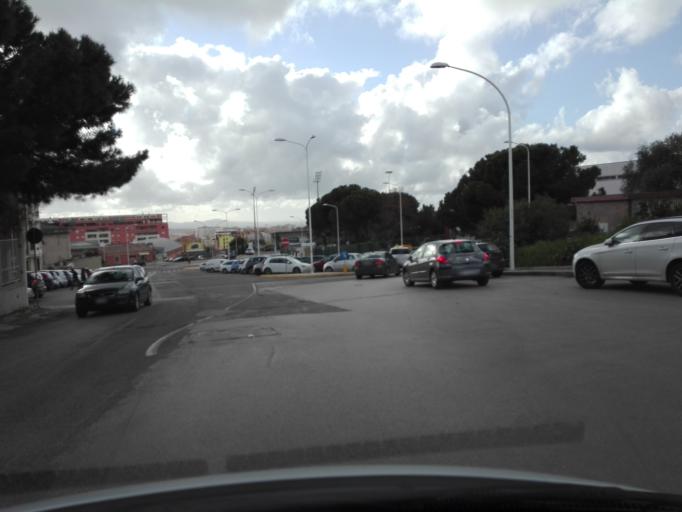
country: IT
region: Sardinia
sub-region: Provincia di Sassari
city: Sassari
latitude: 40.7161
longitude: 8.5837
